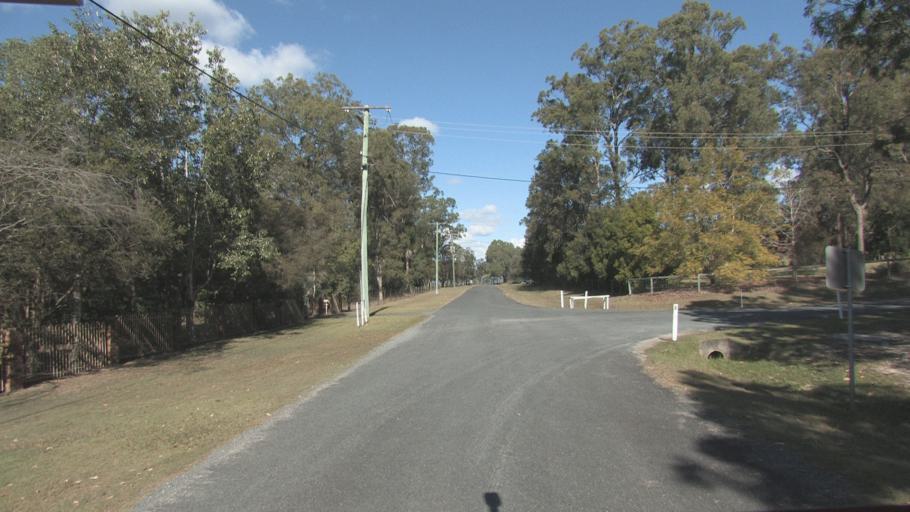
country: AU
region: Queensland
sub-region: Logan
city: Chambers Flat
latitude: -27.7473
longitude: 153.0996
